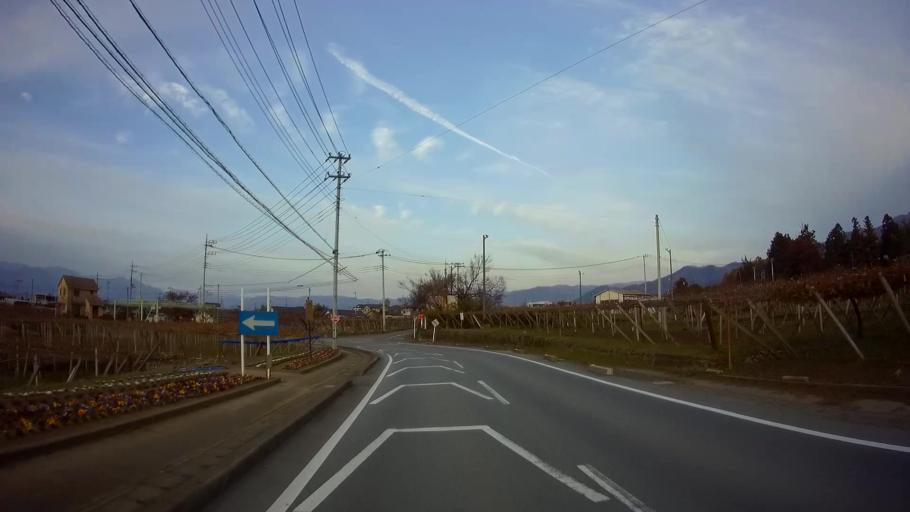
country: JP
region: Yamanashi
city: Isawa
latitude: 35.6162
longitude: 138.6765
